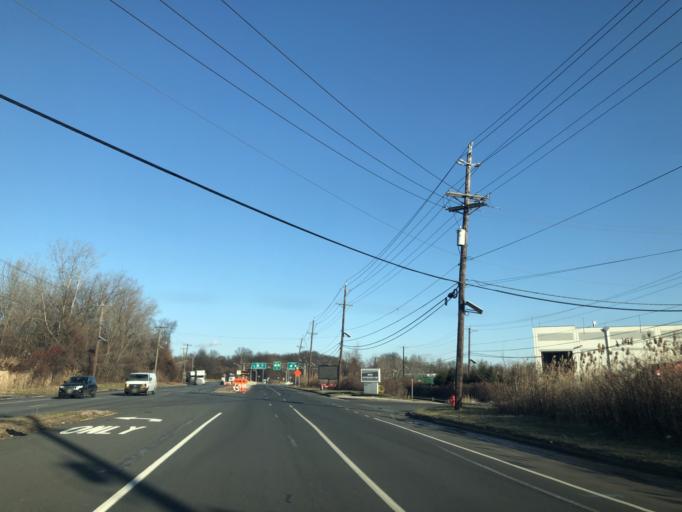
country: US
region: New Jersey
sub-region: Middlesex County
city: Fords
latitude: 40.5188
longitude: -74.3168
